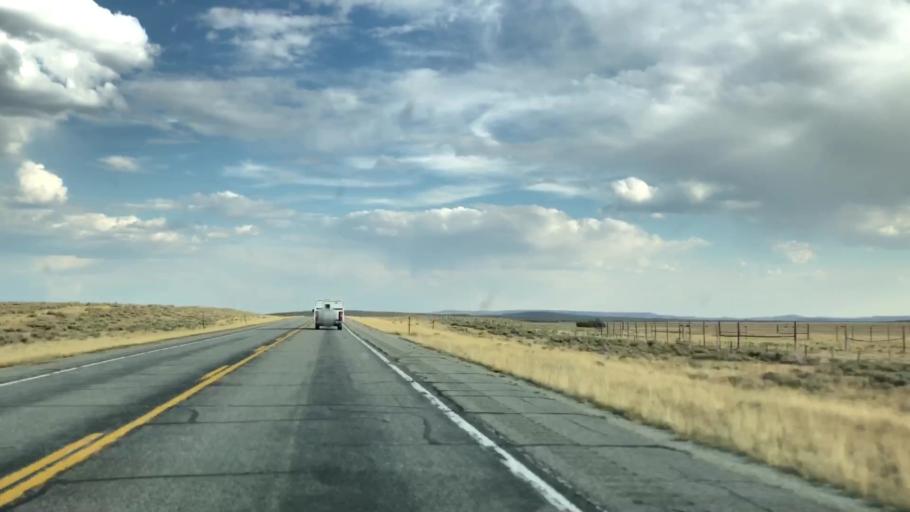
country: US
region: Wyoming
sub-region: Sublette County
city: Pinedale
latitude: 43.0393
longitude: -110.1377
